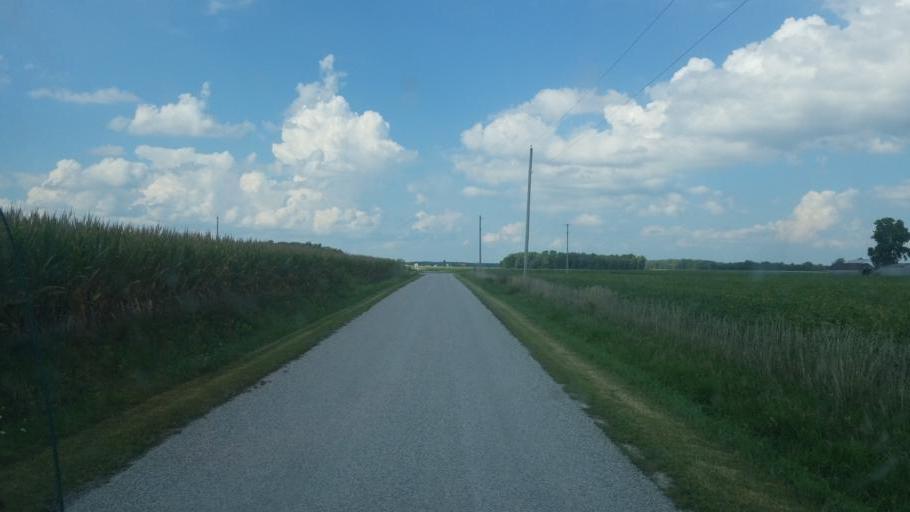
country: US
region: Ohio
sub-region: Huron County
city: Willard
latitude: 40.9949
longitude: -82.7965
